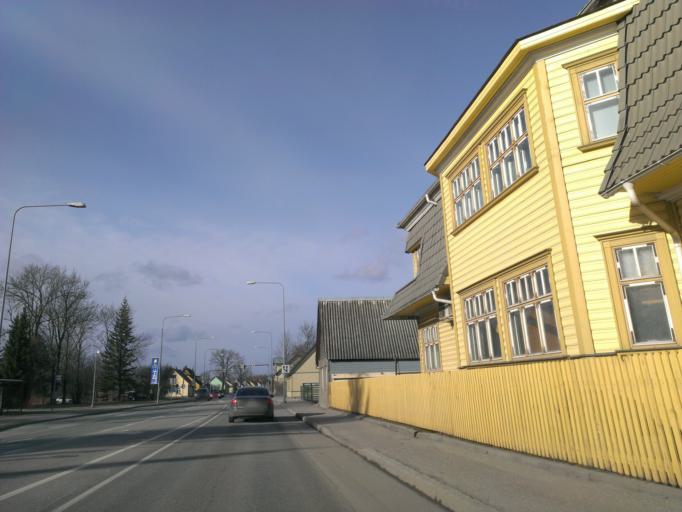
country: EE
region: Paernumaa
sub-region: Paernu linn
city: Parnu
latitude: 58.3980
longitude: 24.4937
